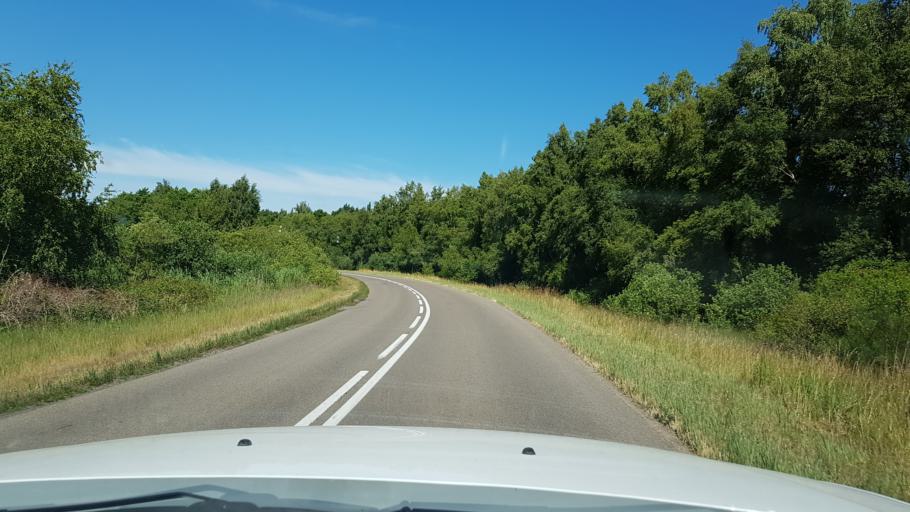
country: PL
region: West Pomeranian Voivodeship
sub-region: Powiat kolobrzeski
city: Grzybowo
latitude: 54.1633
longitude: 15.4801
